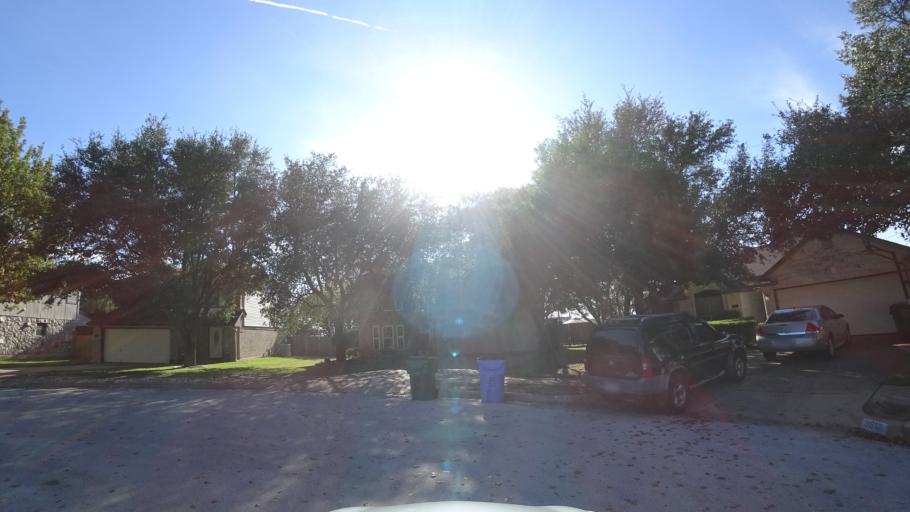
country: US
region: Texas
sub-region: Travis County
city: Wells Branch
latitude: 30.4595
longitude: -97.6895
